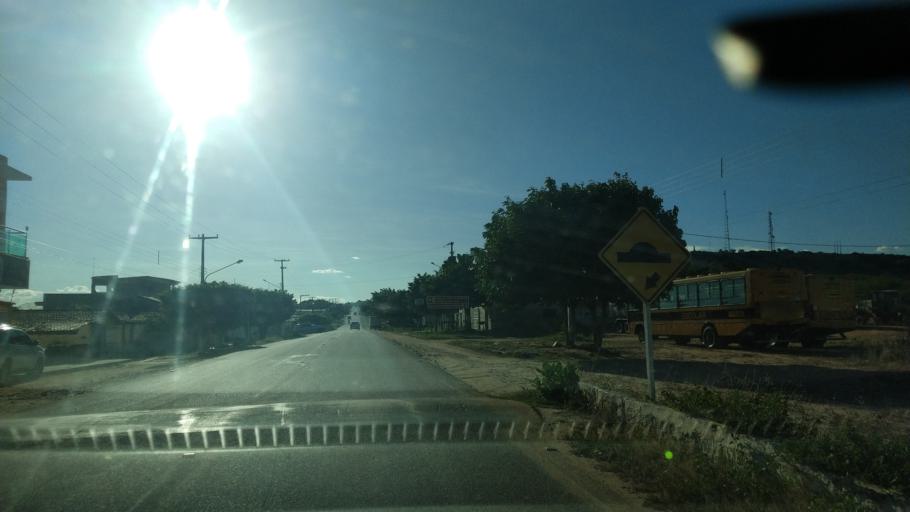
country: BR
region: Rio Grande do Norte
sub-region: Sao Jose Do Campestre
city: Sao Jose do Campestre
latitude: -6.3202
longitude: -35.7057
